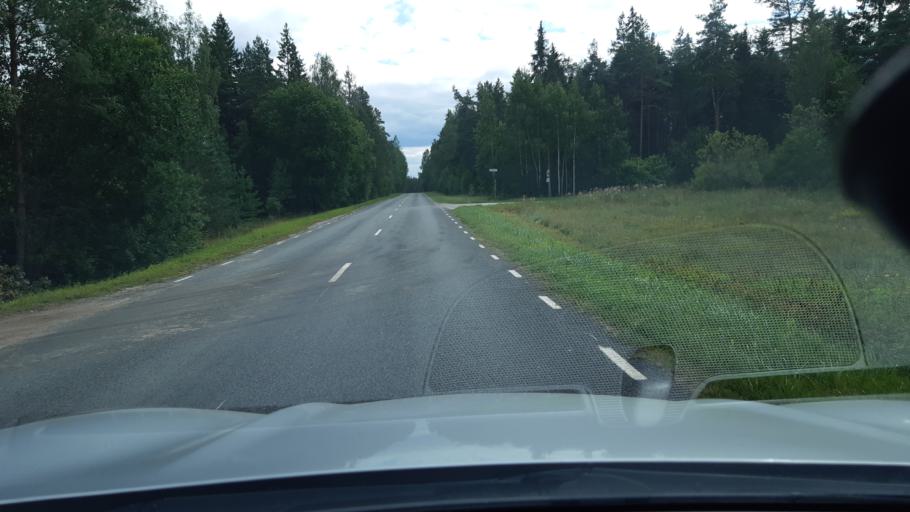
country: EE
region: Raplamaa
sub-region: Maerjamaa vald
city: Marjamaa
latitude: 59.0337
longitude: 24.5523
